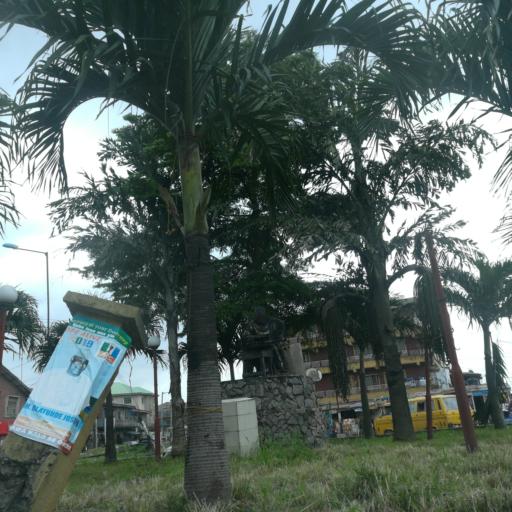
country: NG
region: Lagos
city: Mushin
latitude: 6.5313
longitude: 3.3409
